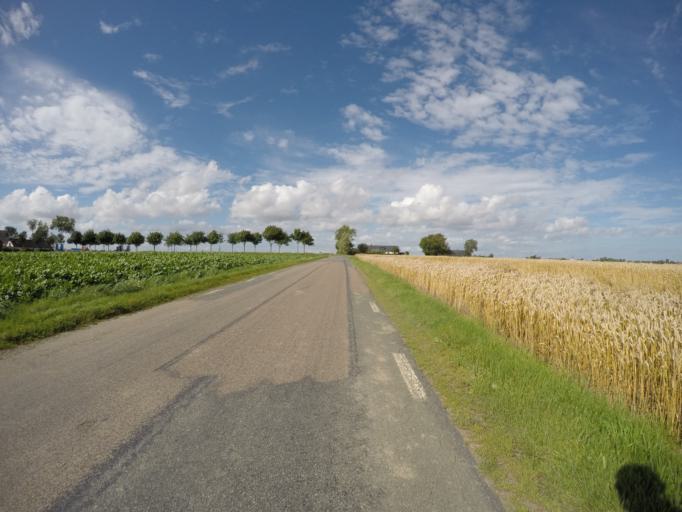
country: SE
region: Skane
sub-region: Simrishamns Kommun
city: Simrishamn
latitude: 55.4899
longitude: 14.1946
